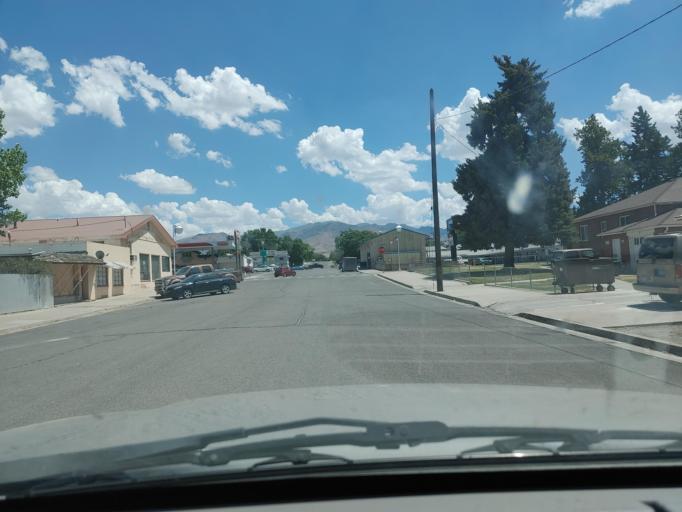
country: US
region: Nevada
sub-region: Humboldt County
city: Winnemucca
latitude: 40.9696
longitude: -117.7409
